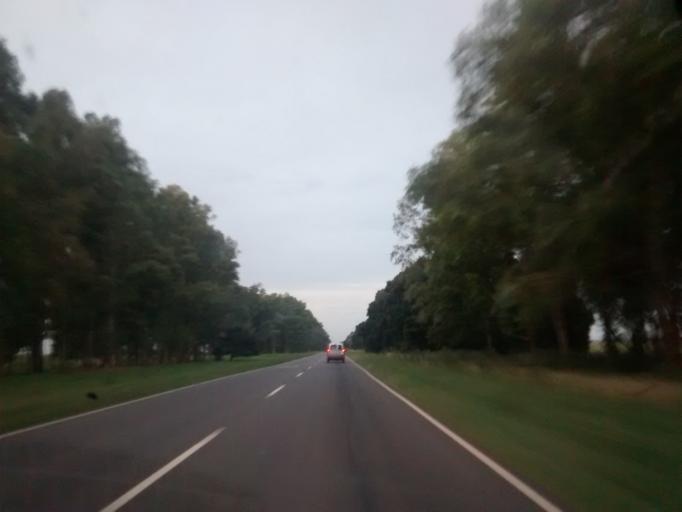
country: AR
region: Buenos Aires
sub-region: Partido de General Belgrano
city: General Belgrano
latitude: -35.6687
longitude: -58.4755
